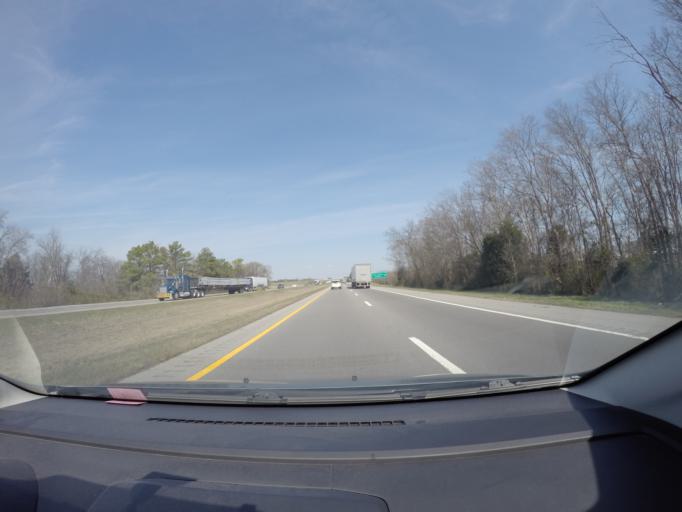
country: US
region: Tennessee
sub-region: Rutherford County
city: Murfreesboro
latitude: 35.7798
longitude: -86.3689
